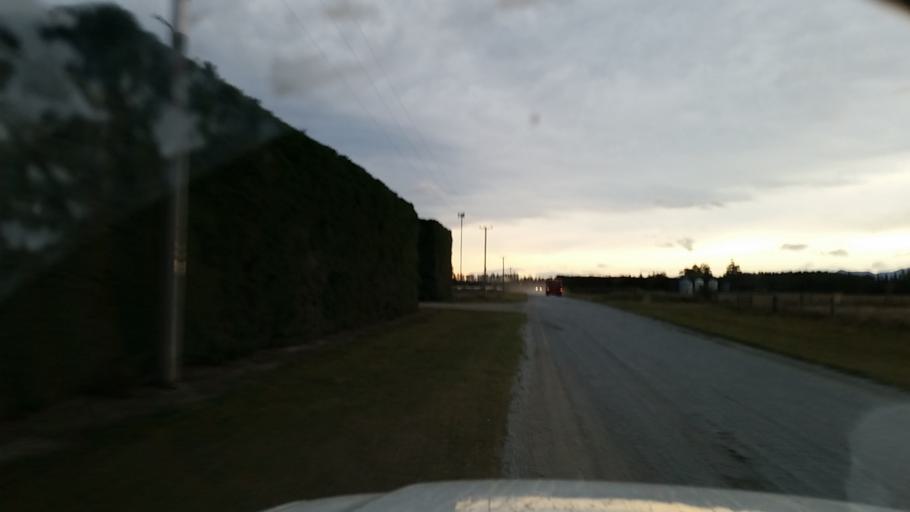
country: NZ
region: Canterbury
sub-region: Ashburton District
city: Tinwald
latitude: -43.8348
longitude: 171.6187
